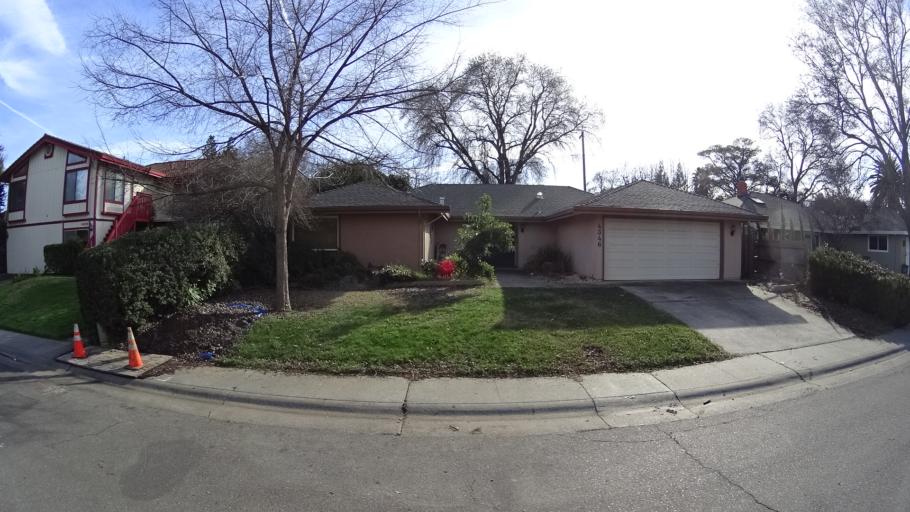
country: US
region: California
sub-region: Yolo County
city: Davis
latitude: 38.5463
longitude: -121.6979
